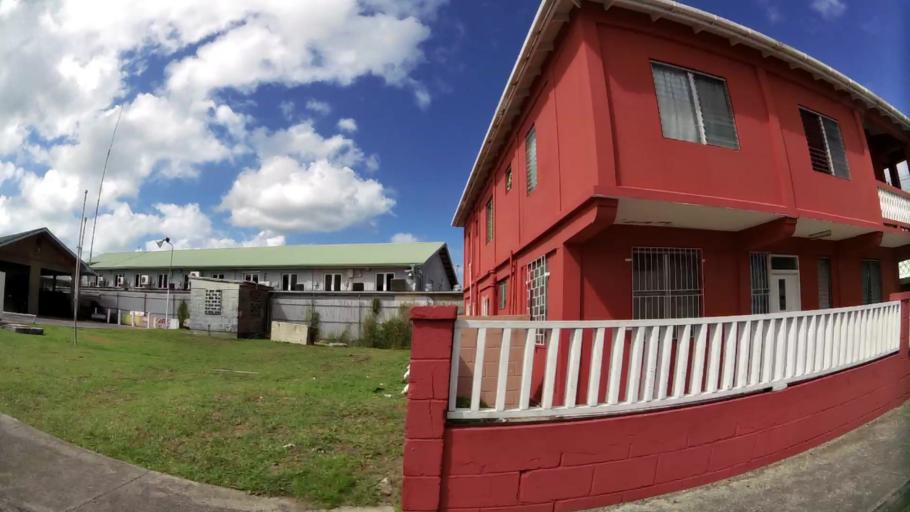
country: AG
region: Saint John
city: Saint John's
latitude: 17.1131
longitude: -61.8395
